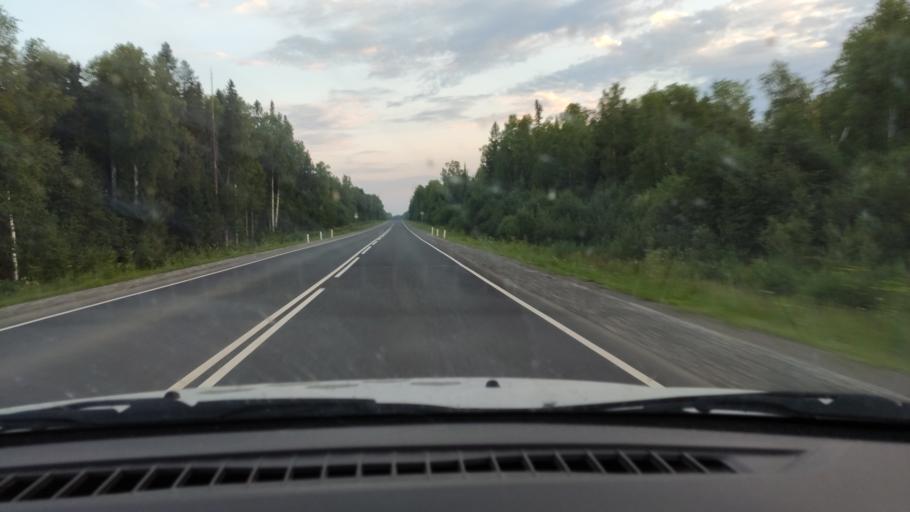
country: RU
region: Perm
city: Zyukayka
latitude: 58.3438
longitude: 54.7133
